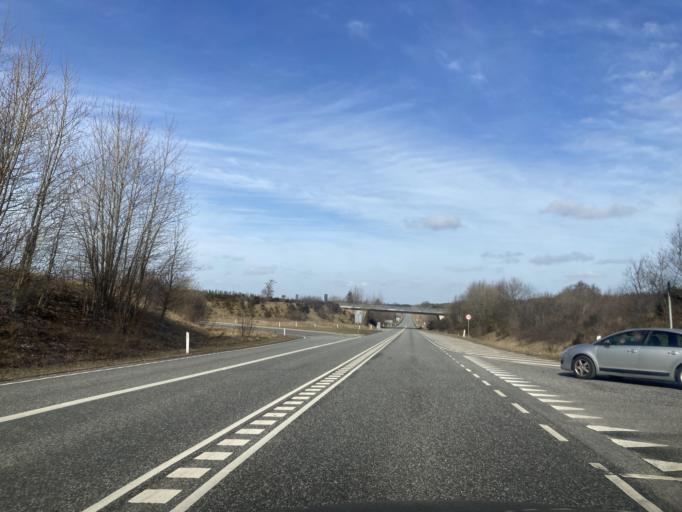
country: DK
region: Central Jutland
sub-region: Hedensted Kommune
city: Torring
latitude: 55.9677
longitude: 9.4037
